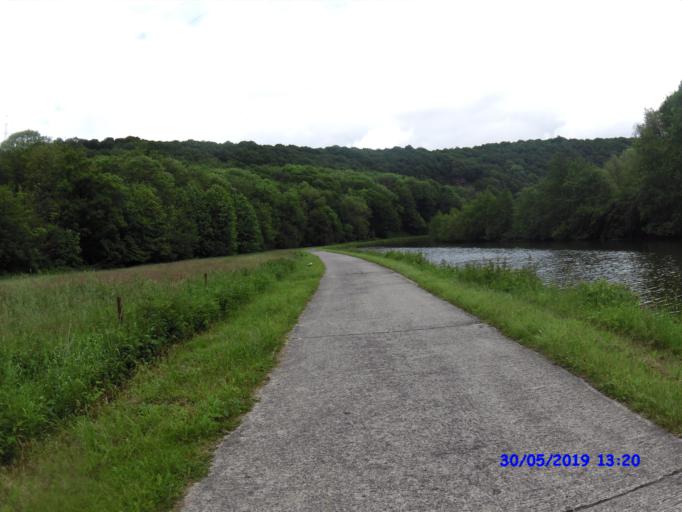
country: BE
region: Wallonia
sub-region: Province du Hainaut
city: Thuin
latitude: 50.3733
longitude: 4.3228
